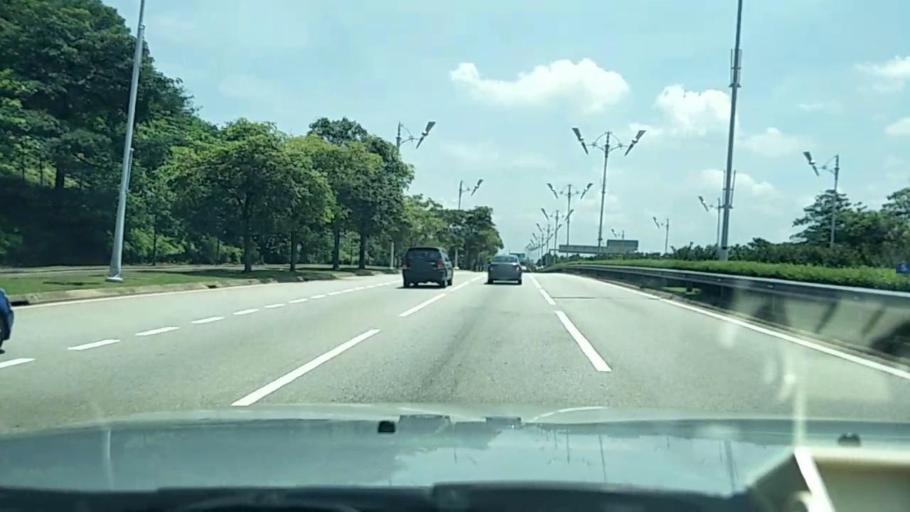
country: MY
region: Putrajaya
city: Putrajaya
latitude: 2.9575
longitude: 101.7110
